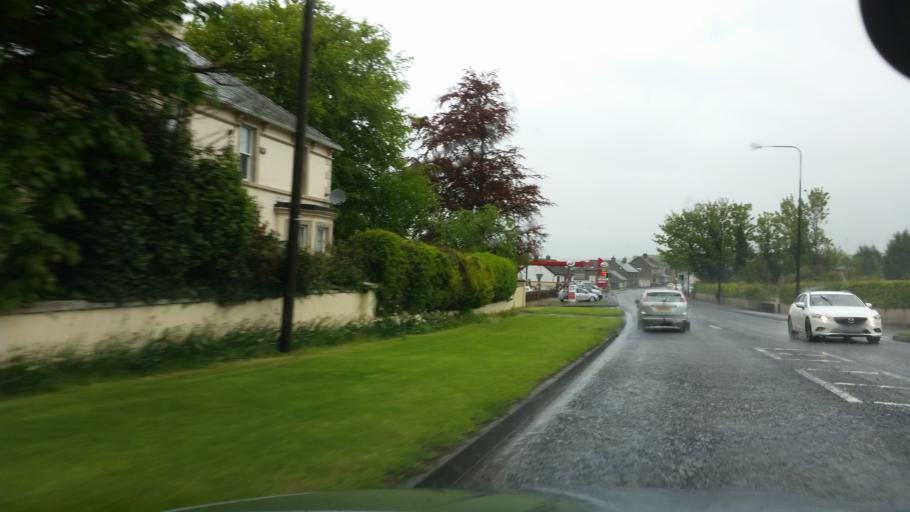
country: GB
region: Northern Ireland
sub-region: Strabane District
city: Strabane
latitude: 54.8580
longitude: -7.4301
